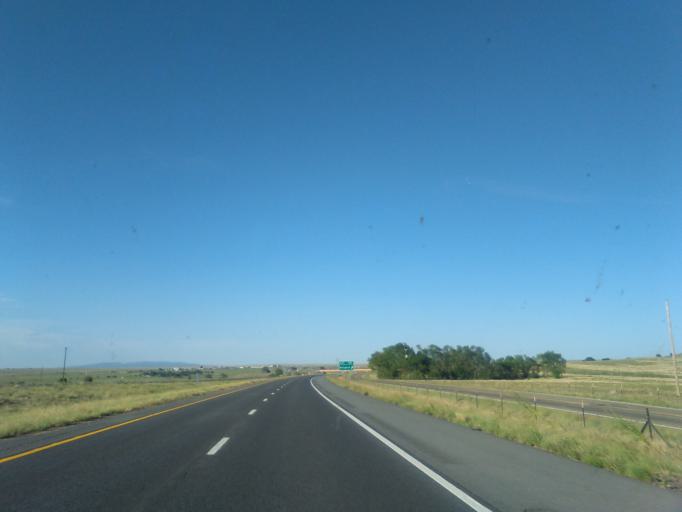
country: US
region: New Mexico
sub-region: San Miguel County
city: Las Vegas
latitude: 35.6736
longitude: -105.1770
